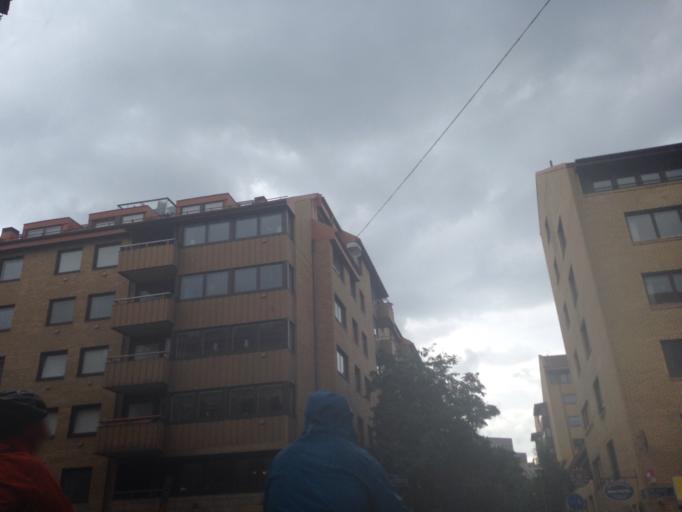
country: SE
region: Vaestra Goetaland
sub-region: Goteborg
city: Goeteborg
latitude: 57.6983
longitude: 11.9470
